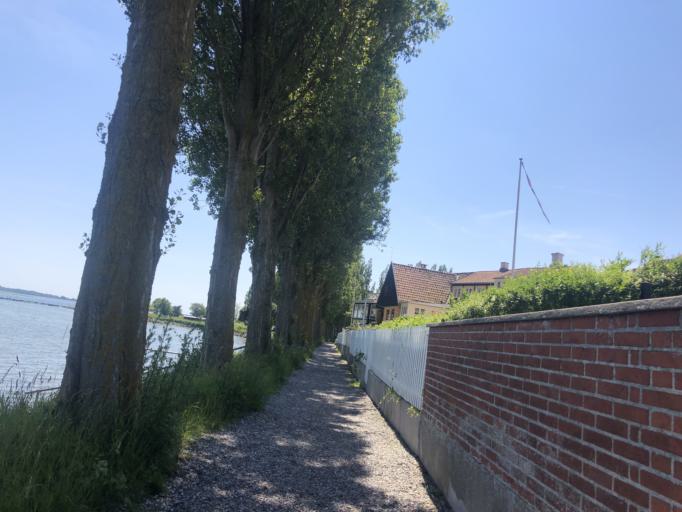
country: DK
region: South Denmark
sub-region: AEro Kommune
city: AEroskobing
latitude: 54.8873
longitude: 10.4142
